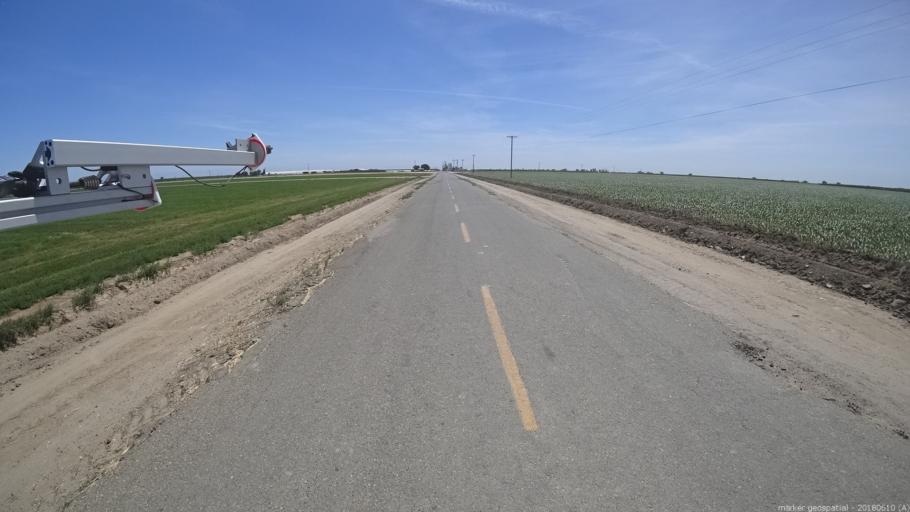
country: US
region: California
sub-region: Merced County
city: Dos Palos
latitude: 37.0545
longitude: -120.4501
